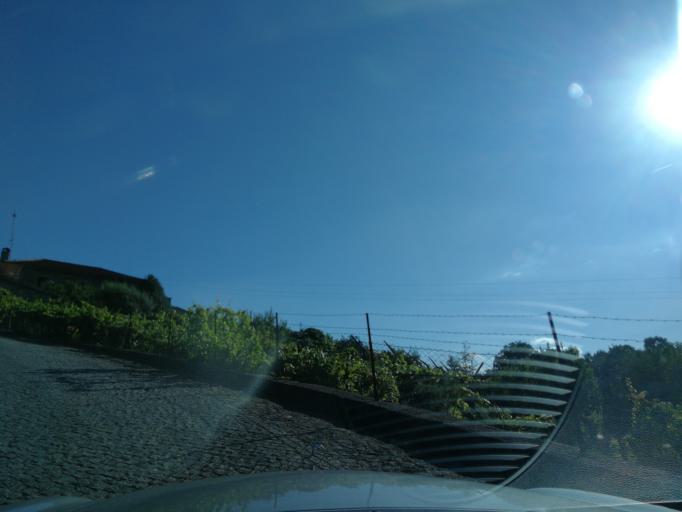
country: PT
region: Braga
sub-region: Braga
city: Adaufe
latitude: 41.5595
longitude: -8.3863
